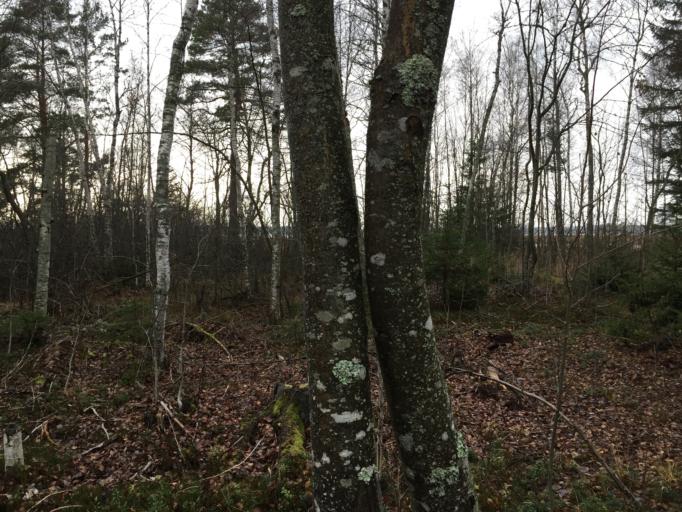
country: SE
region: OErebro
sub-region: Orebro Kommun
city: Odensbacken
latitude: 59.0522
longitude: 15.5527
